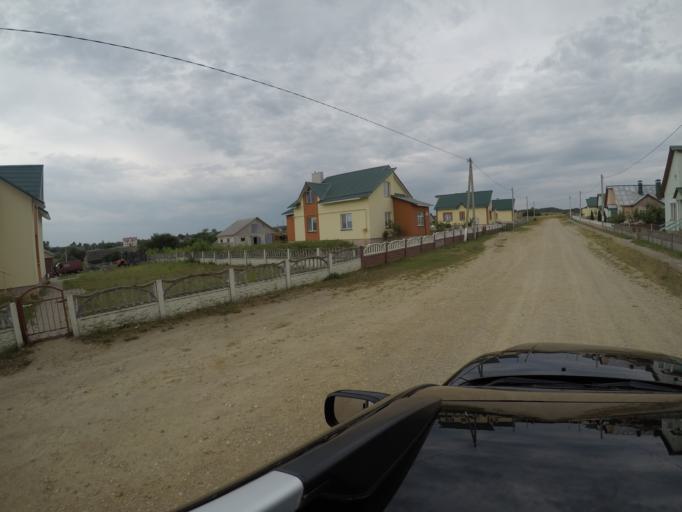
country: BY
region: Grodnenskaya
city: Hal'shany
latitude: 54.2560
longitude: 26.0244
